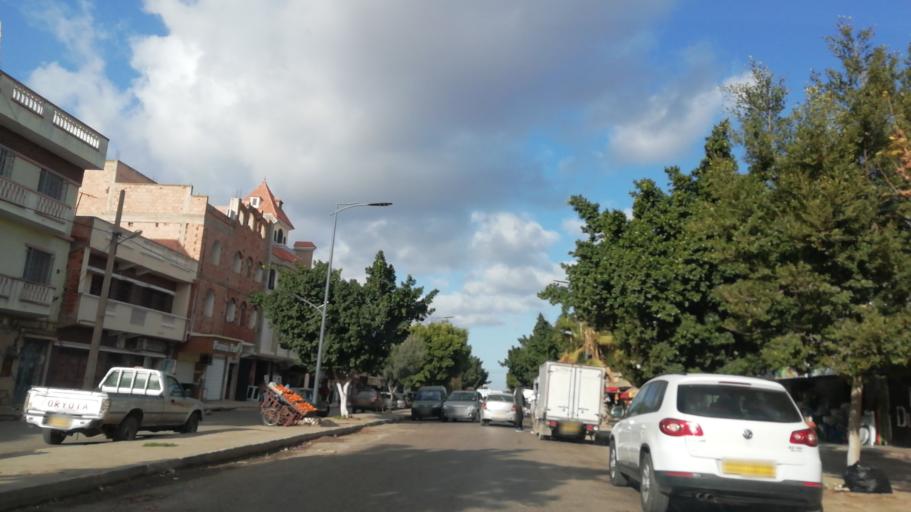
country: DZ
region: Ain Temouchent
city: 'Ain Temouchent
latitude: 35.3015
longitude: -1.1526
